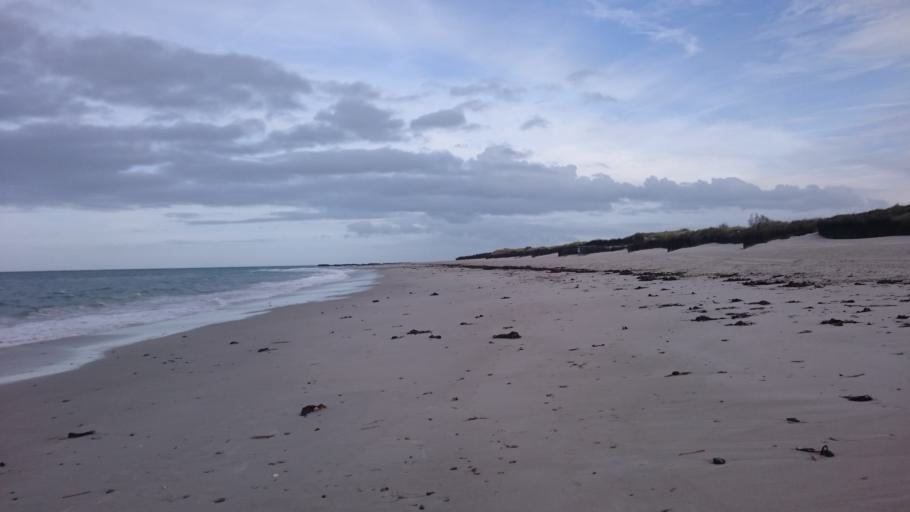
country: DE
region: Schleswig-Holstein
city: Helgoland
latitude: 54.1870
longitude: 7.9075
